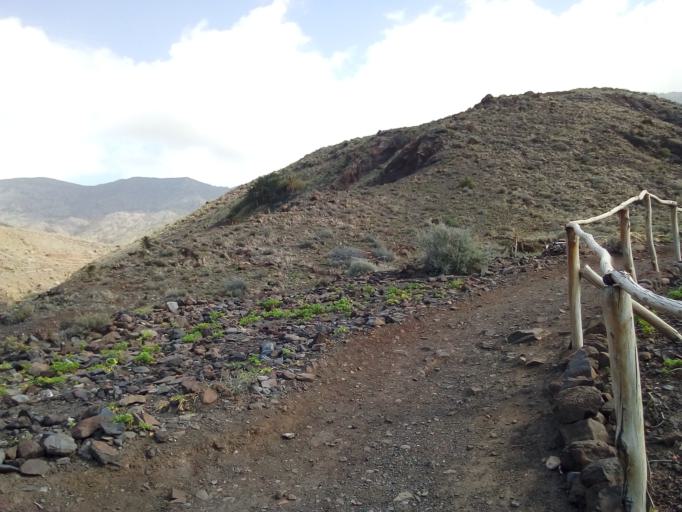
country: ES
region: Canary Islands
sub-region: Provincia de Santa Cruz de Tenerife
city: Vallehermosa
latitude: 28.1718
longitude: -17.3351
